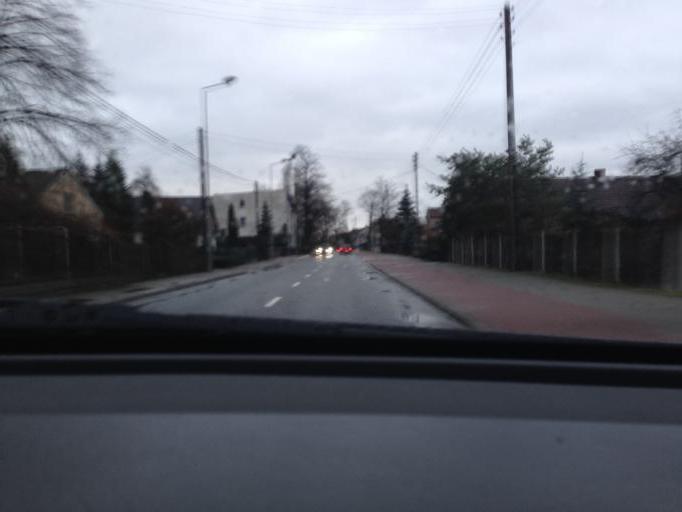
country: PL
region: Opole Voivodeship
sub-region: Powiat opolski
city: Opole
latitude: 50.6880
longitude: 17.9524
